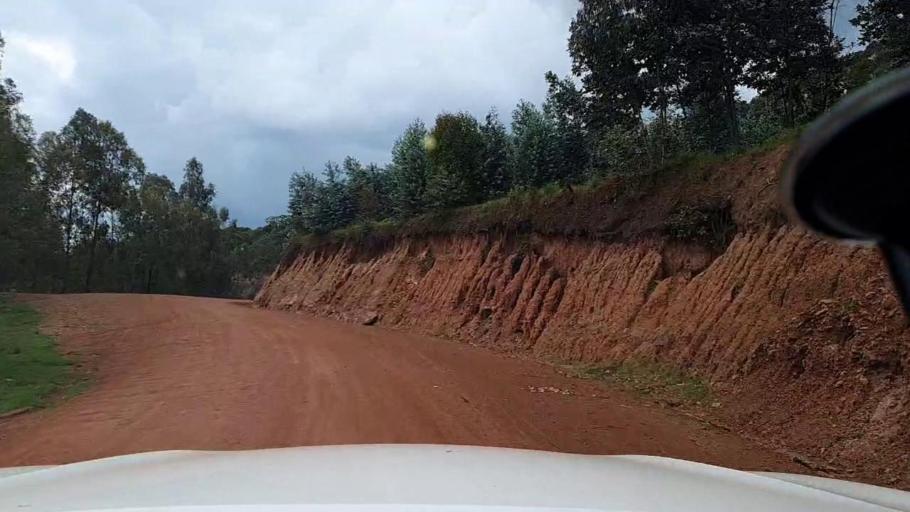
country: RW
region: Kigali
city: Kigali
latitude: -1.7602
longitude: 29.8447
